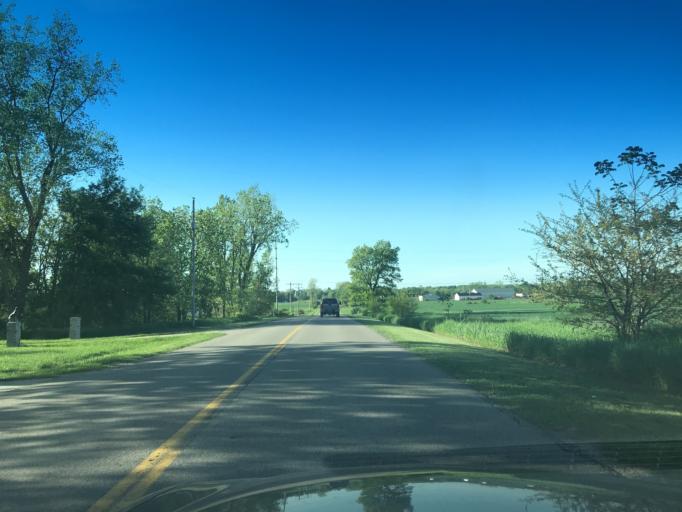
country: US
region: Michigan
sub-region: Ingham County
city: Mason
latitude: 42.5588
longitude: -84.4530
